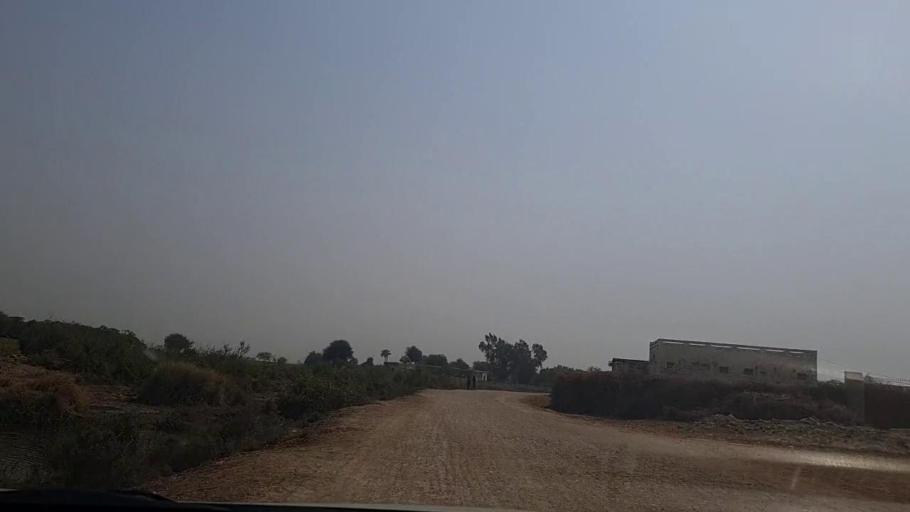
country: PK
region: Sindh
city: Pithoro
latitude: 25.5498
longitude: 69.2490
